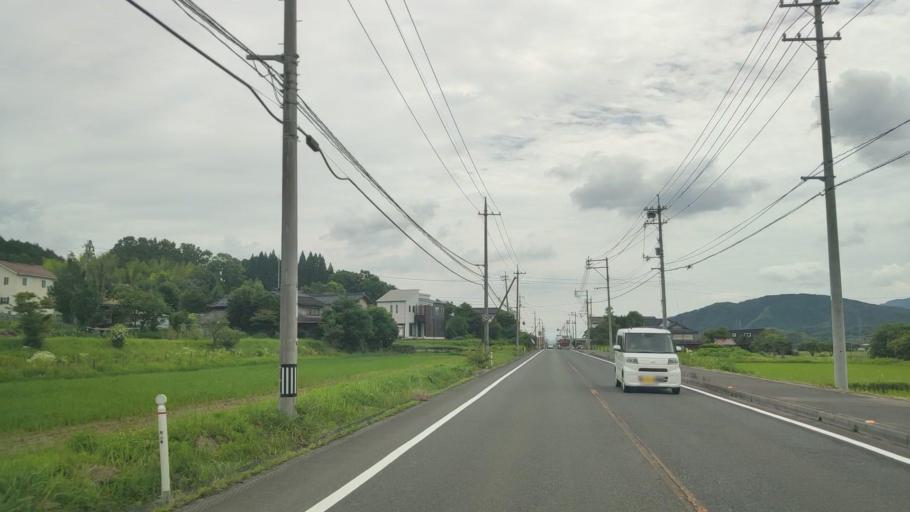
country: JP
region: Okayama
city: Tsuyama
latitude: 35.0556
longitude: 133.9254
